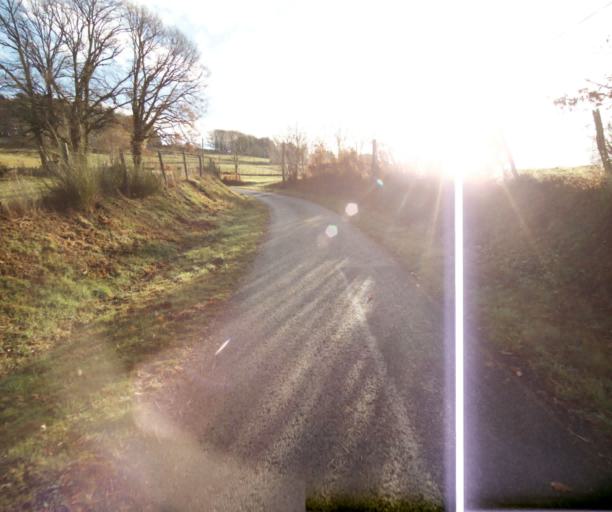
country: FR
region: Limousin
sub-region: Departement de la Correze
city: Saint-Mexant
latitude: 45.2388
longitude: 1.6488
